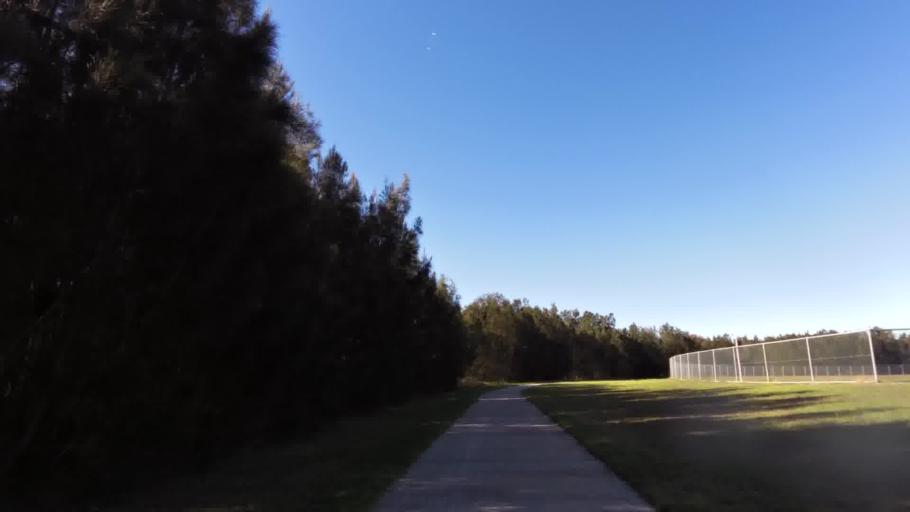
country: AU
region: New South Wales
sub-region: Wollongong
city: Berkeley
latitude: -34.4833
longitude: 150.8386
